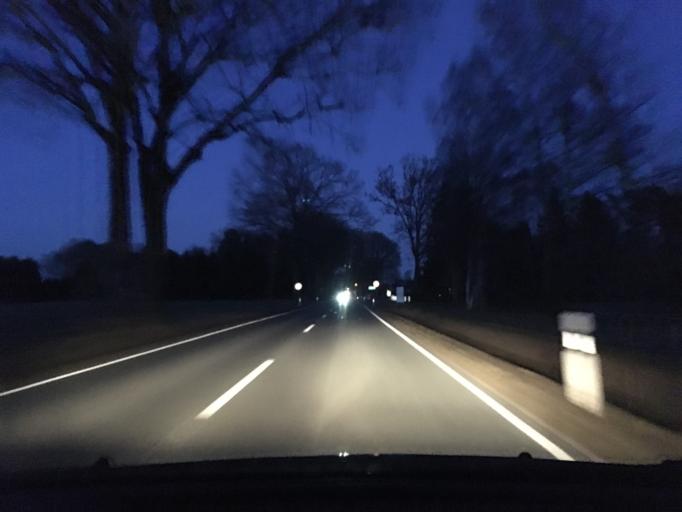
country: DE
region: Lower Saxony
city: Schneverdingen
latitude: 53.1159
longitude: 9.7559
